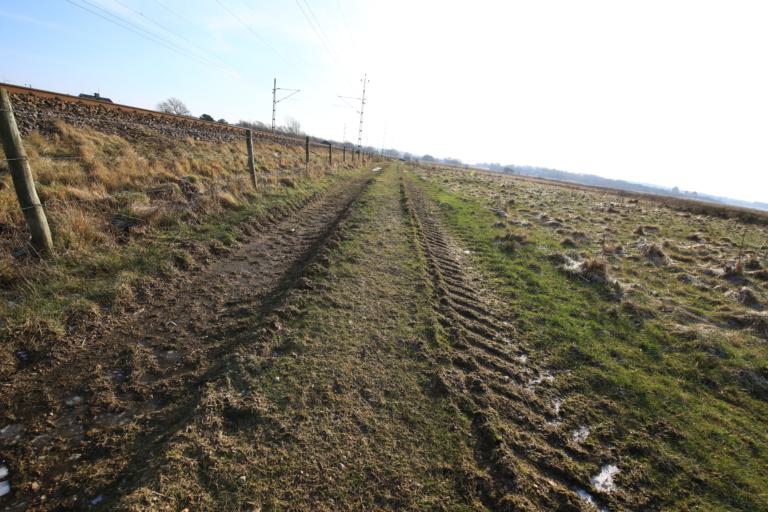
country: SE
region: Halland
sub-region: Varbergs Kommun
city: Veddige
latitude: 57.2183
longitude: 12.2191
